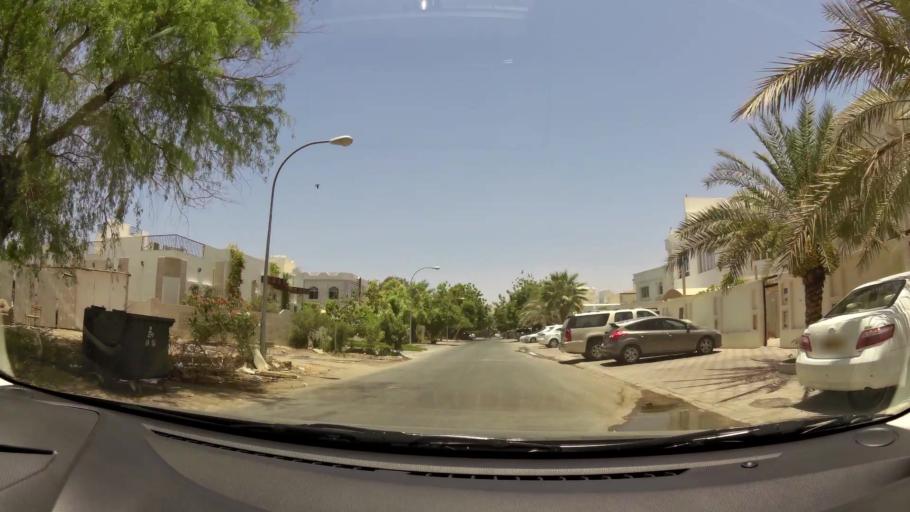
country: OM
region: Muhafazat Masqat
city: Bawshar
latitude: 23.5936
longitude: 58.3924
